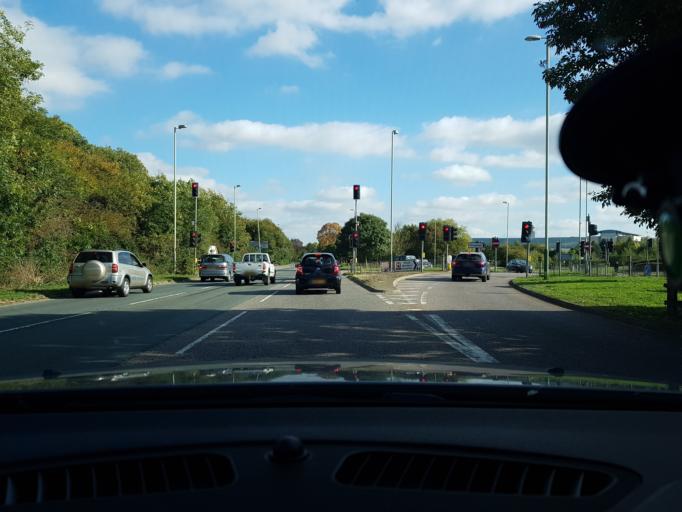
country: GB
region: England
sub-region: Borough of Swindon
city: Chiseldon
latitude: 51.5421
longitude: -1.7289
